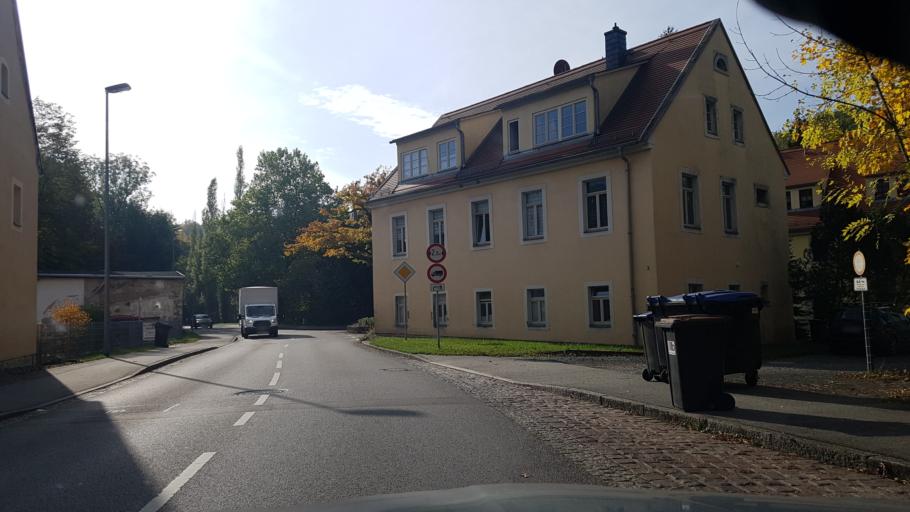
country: DE
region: Saxony
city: Dohma
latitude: 50.9241
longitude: 13.9618
